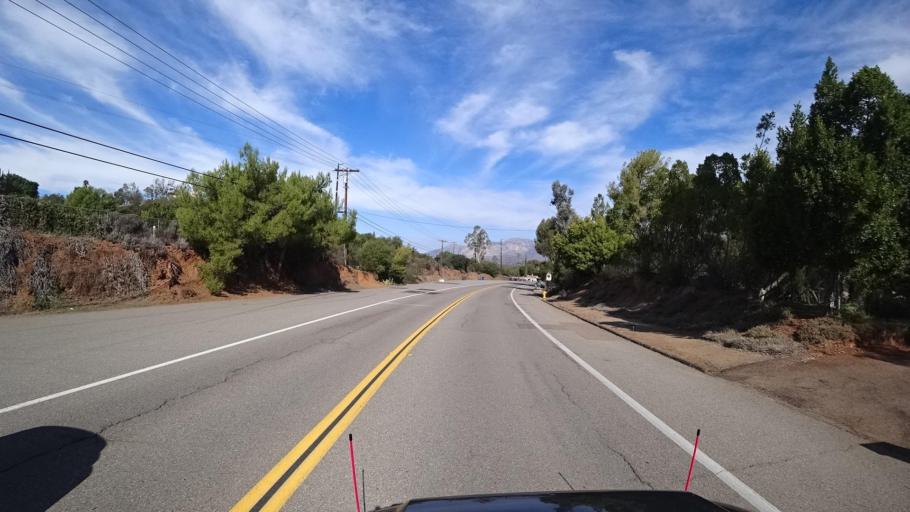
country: US
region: California
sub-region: San Diego County
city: Alpine
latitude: 32.8246
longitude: -116.7888
